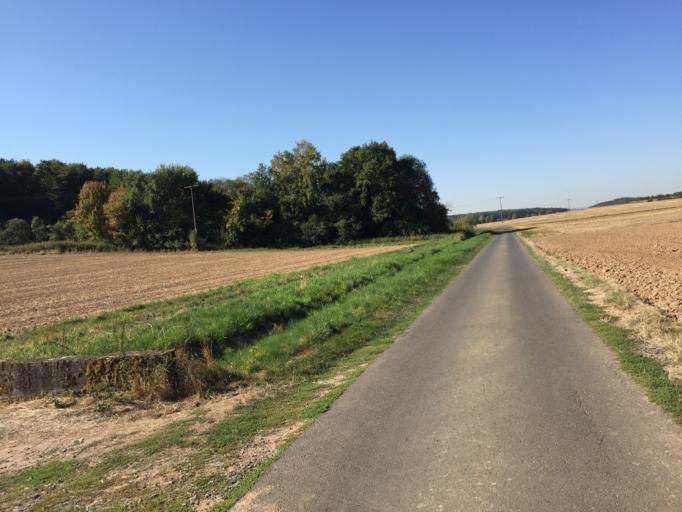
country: DE
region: Hesse
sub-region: Regierungsbezirk Darmstadt
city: Nidda
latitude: 50.4331
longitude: 8.9626
